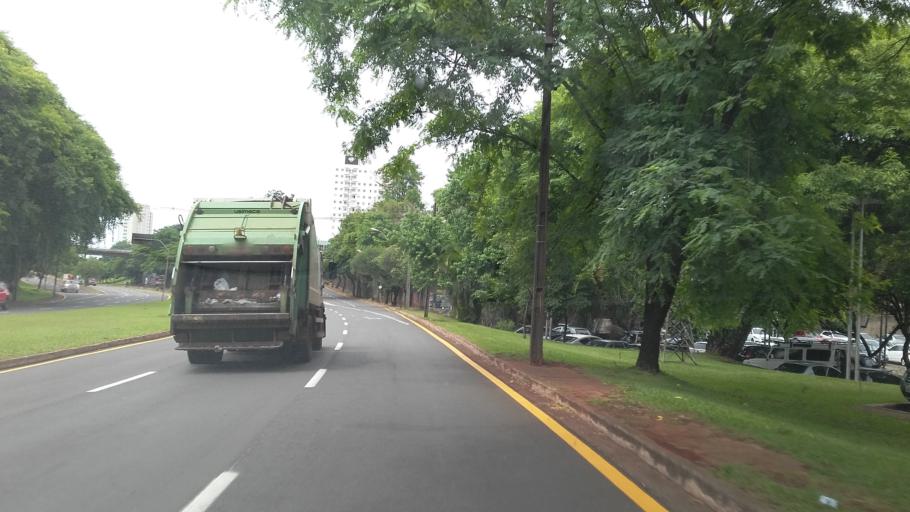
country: BR
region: Parana
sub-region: Londrina
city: Londrina
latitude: -23.3168
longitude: -51.1507
